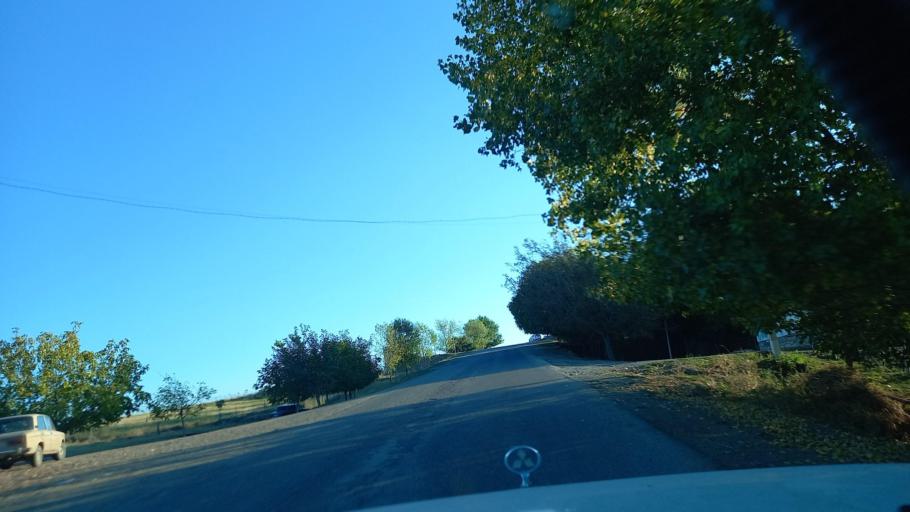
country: AZ
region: Shamkir Rayon
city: Shamkhor
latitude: 40.7723
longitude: 45.9584
